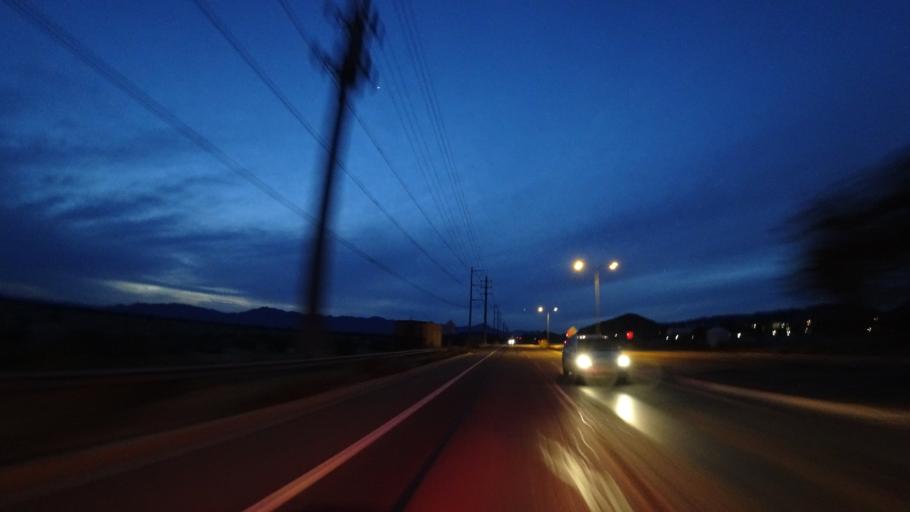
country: US
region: Arizona
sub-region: Maricopa County
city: Guadalupe
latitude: 33.2910
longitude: -112.0332
